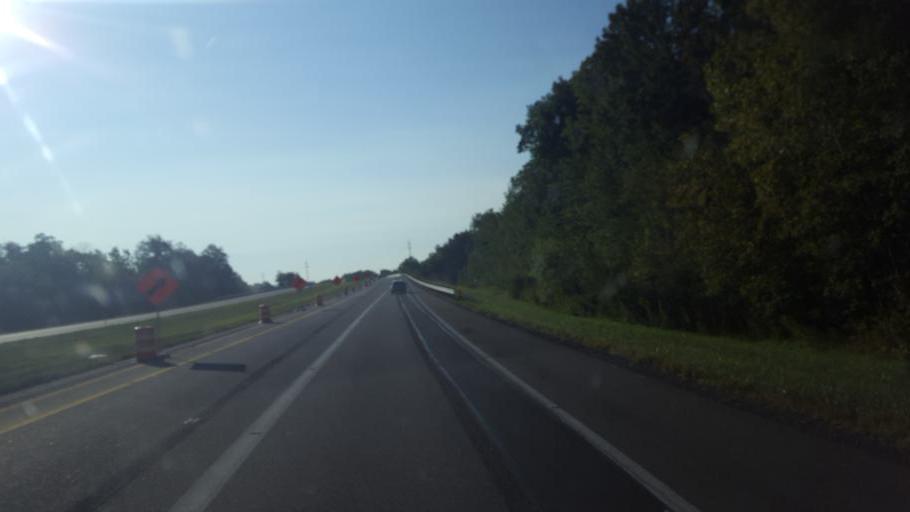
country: US
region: Ohio
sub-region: Cuyahoga County
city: Solon
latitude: 41.3933
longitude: -81.4254
